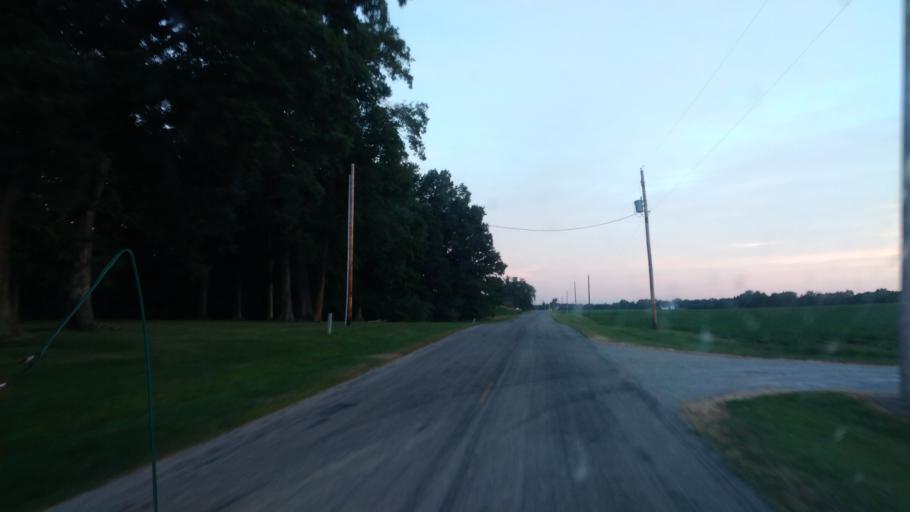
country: US
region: Indiana
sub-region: Wells County
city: Bluffton
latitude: 40.6746
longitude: -85.1297
